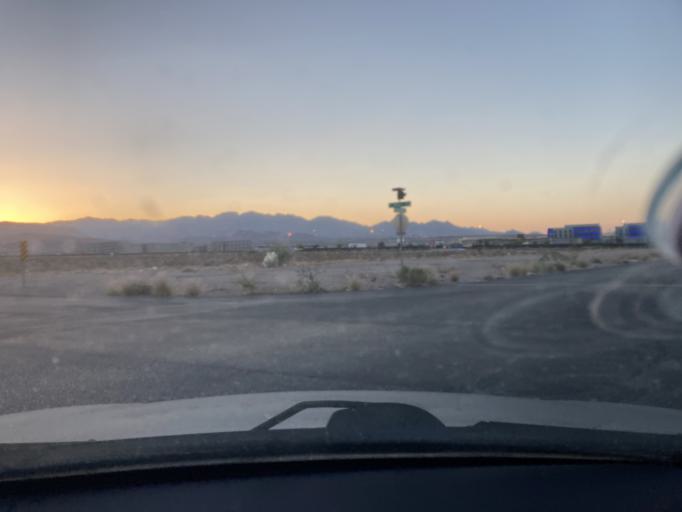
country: US
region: Nevada
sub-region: Clark County
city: Enterprise
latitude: 36.0592
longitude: -115.2701
